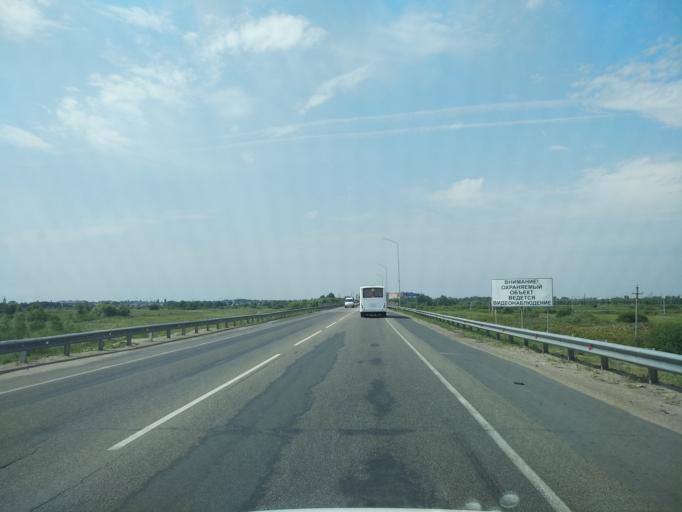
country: RU
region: Voronezj
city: Somovo
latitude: 51.6859
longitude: 39.3526
